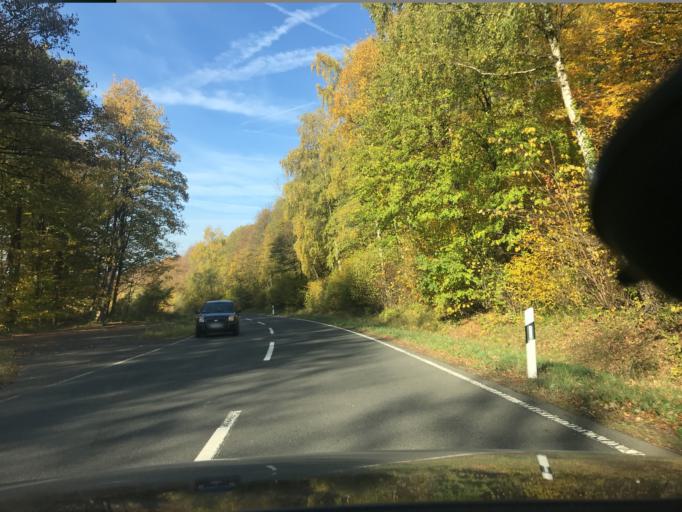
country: DE
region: Hesse
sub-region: Regierungsbezirk Kassel
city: Grossalmerode
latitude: 51.2127
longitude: 9.8277
